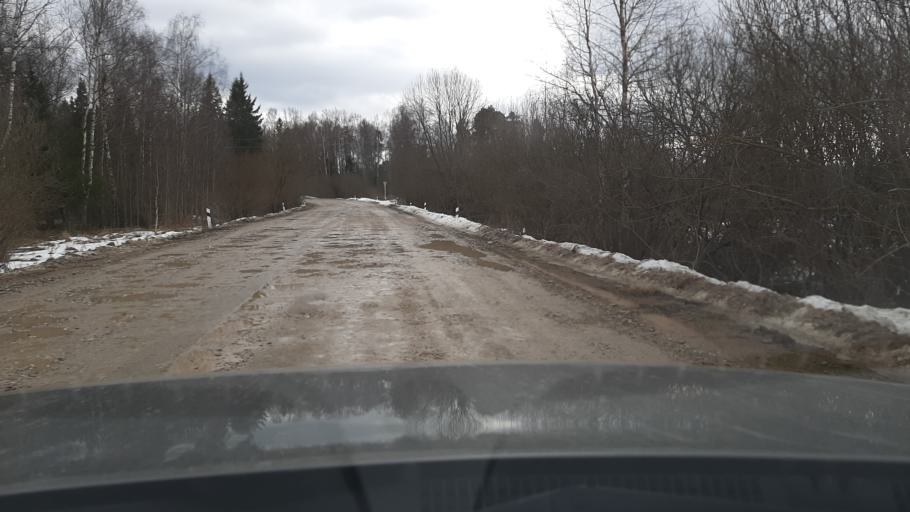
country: RU
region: Ivanovo
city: Teykovo
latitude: 56.8867
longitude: 40.6182
